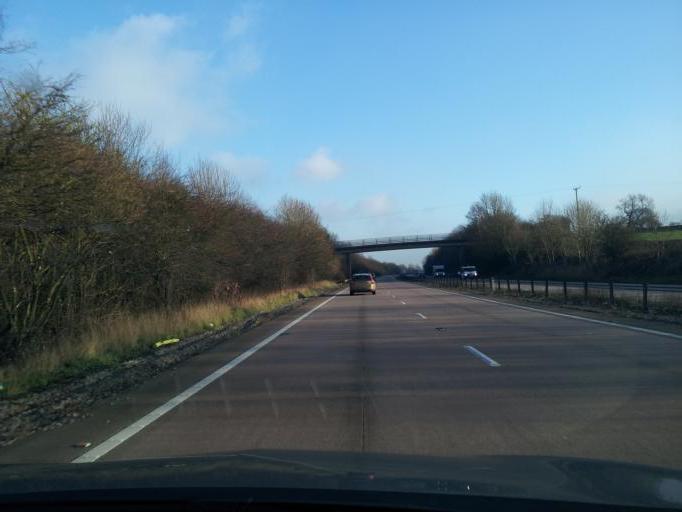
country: GB
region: England
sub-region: Staffordshire
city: Uttoxeter
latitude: 52.9207
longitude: -1.9226
